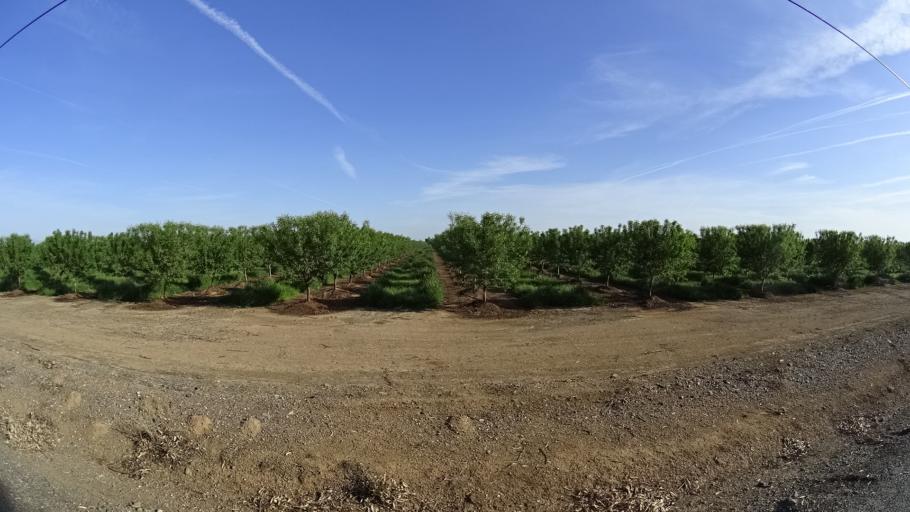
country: US
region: California
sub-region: Glenn County
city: Orland
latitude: 39.7188
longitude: -122.2267
